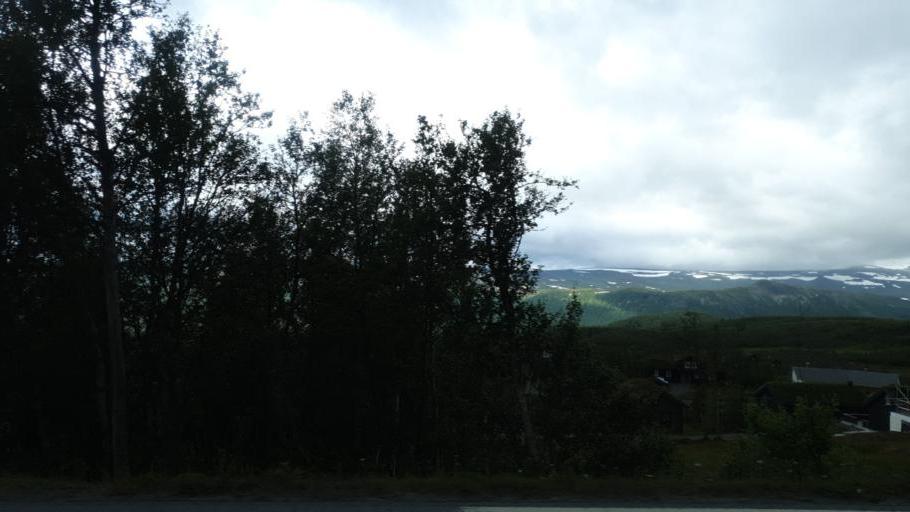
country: NO
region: Oppland
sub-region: Vestre Slidre
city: Slidre
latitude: 61.2546
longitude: 8.8778
